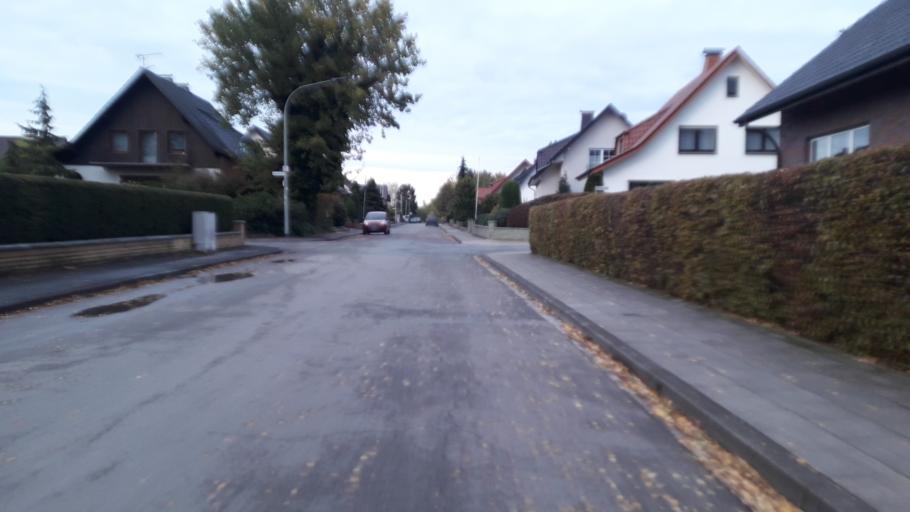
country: DE
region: North Rhine-Westphalia
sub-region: Regierungsbezirk Detmold
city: Delbruck
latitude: 51.7405
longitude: 8.6212
